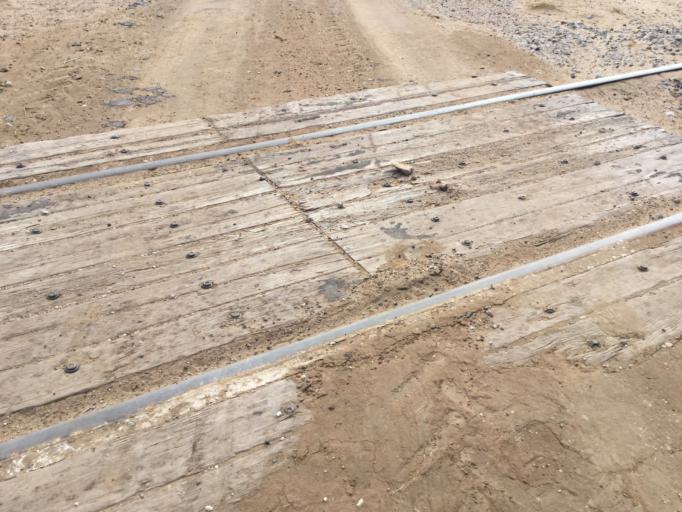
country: US
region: Kansas
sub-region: Morton County
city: Elkhart
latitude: 37.0883
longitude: -101.7365
